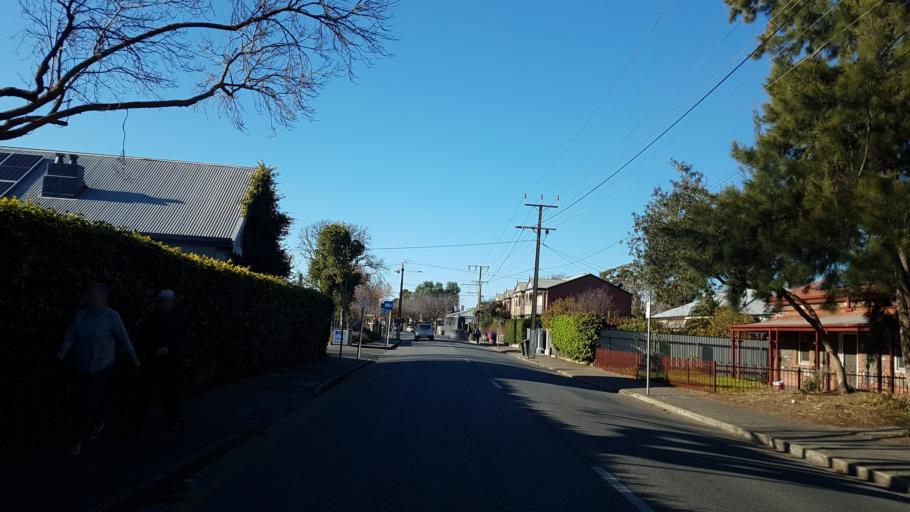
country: AU
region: South Australia
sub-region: Norwood Payneham St Peters
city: Royston Park
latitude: -34.9094
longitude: 138.6151
